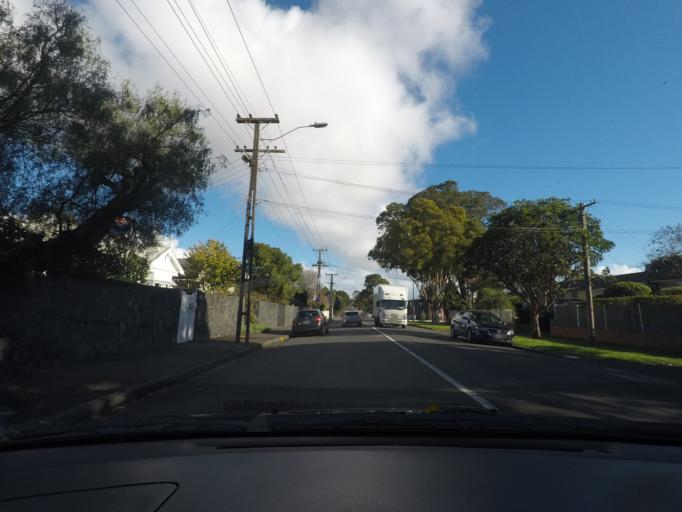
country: NZ
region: Auckland
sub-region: Auckland
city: Auckland
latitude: -36.8854
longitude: 174.7810
